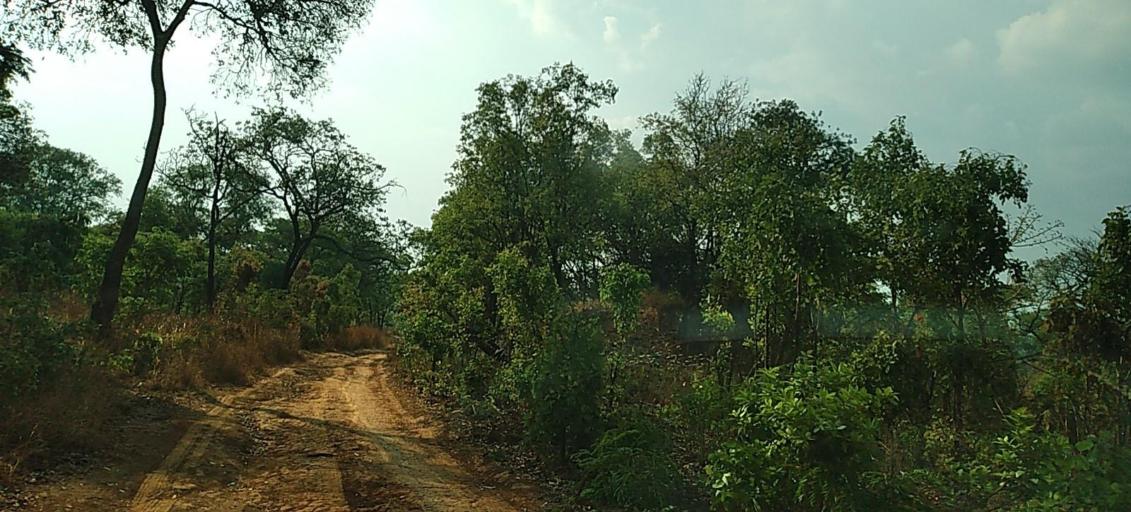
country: ZM
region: North-Western
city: Solwezi
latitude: -12.0681
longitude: 26.1804
